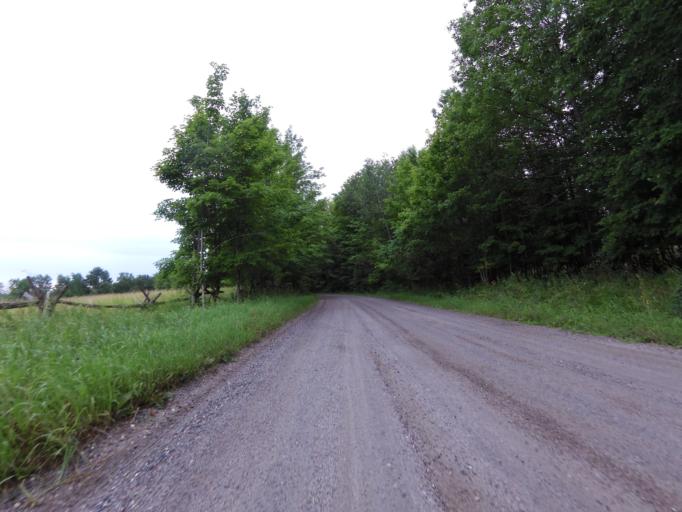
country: CA
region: Ontario
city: Perth
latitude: 45.0435
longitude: -76.3958
